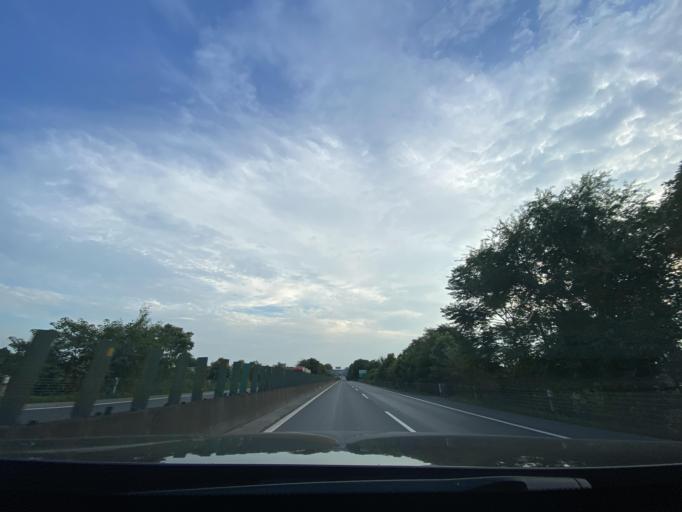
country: CN
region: Sichuan
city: Luojiang
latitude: 31.3683
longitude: 104.5404
